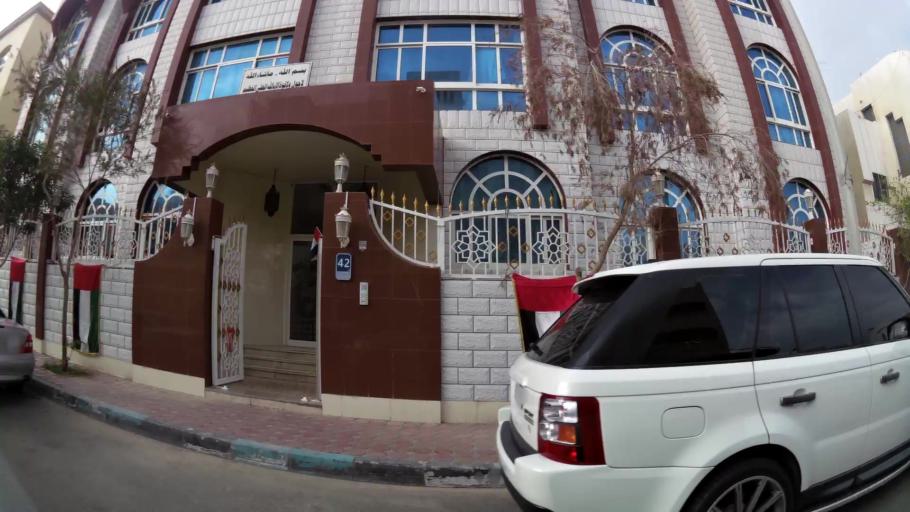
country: AE
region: Abu Dhabi
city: Abu Dhabi
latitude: 24.4647
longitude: 54.3780
